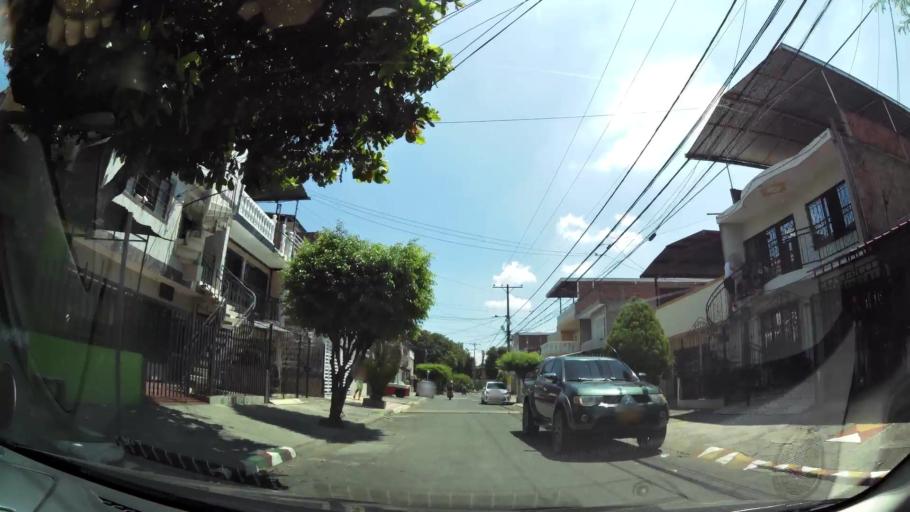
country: CO
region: Valle del Cauca
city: Cali
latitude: 3.4401
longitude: -76.4961
